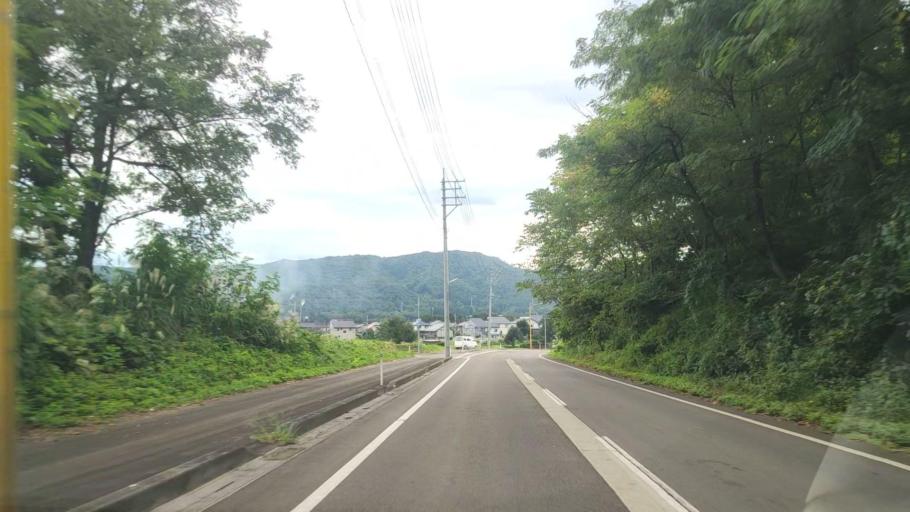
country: JP
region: Niigata
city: Arai
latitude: 37.0122
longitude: 138.2551
